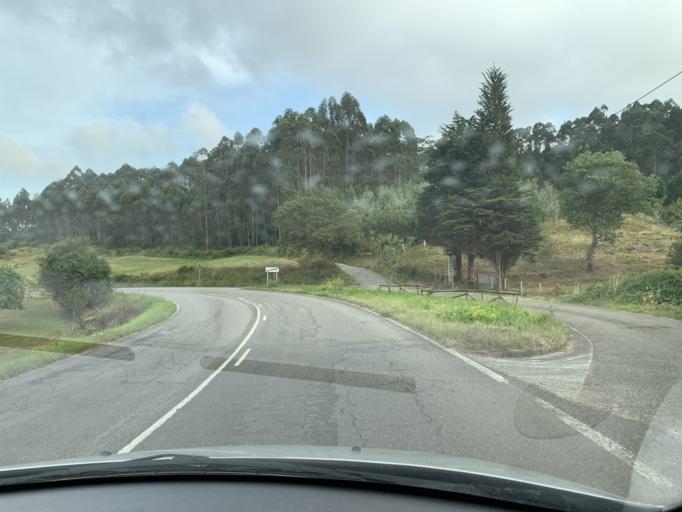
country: ES
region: Asturias
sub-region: Province of Asturias
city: Villaviciosa
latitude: 43.5184
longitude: -5.4384
